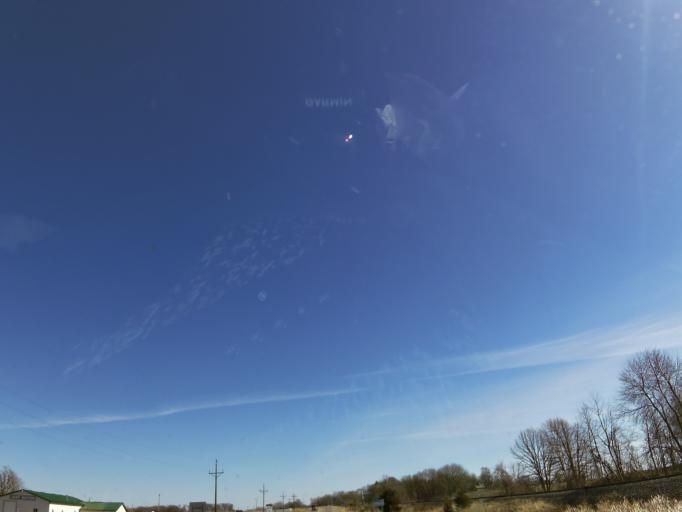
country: US
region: Minnesota
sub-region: Wright County
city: Annandale
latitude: 45.2462
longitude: -94.0823
